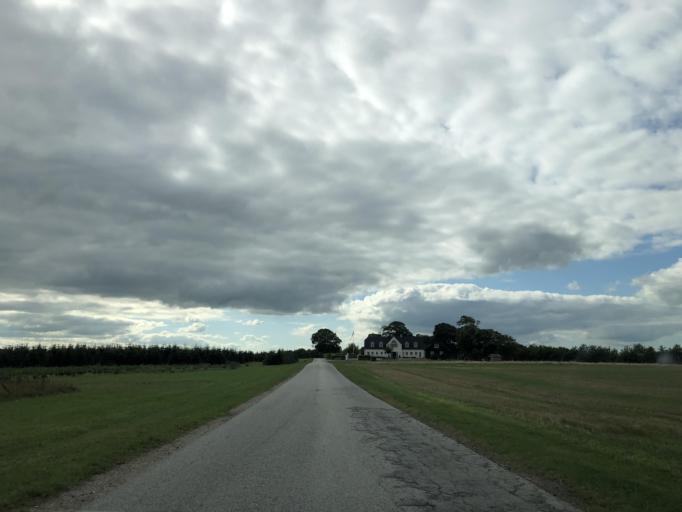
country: DK
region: North Denmark
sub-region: Alborg Kommune
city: Nibe
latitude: 56.8445
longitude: 9.6925
